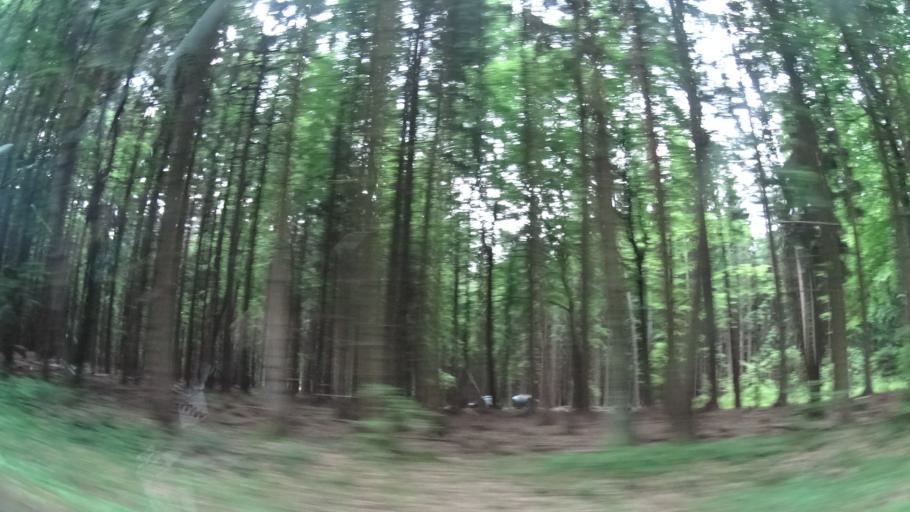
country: DE
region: Hesse
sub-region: Regierungsbezirk Darmstadt
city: Lutzelbach
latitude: 49.7063
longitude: 9.0846
